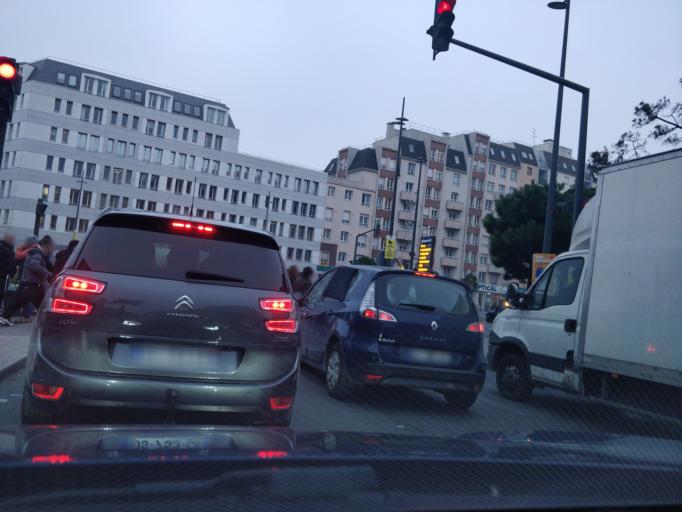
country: FR
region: Ile-de-France
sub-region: Departement du Val-de-Marne
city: Le Kremlin-Bicetre
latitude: 48.8096
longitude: 2.3619
